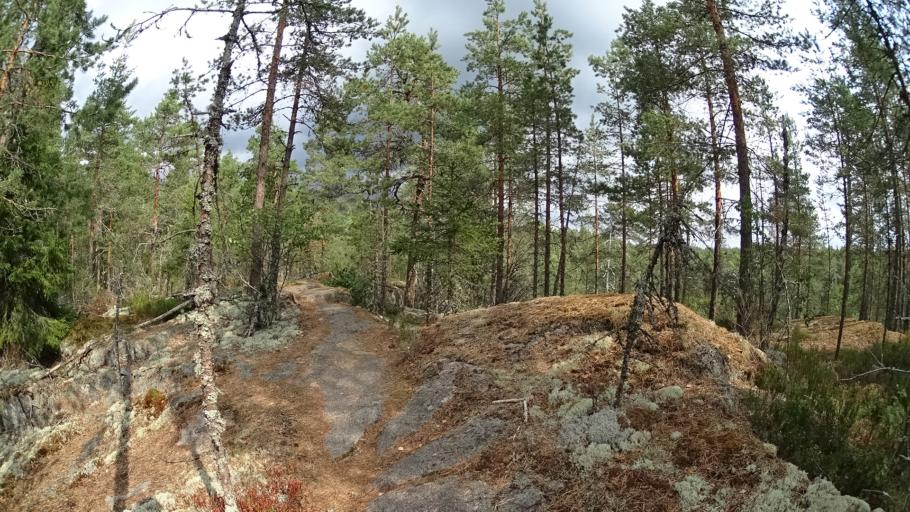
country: FI
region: Uusimaa
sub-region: Helsinki
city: Espoo
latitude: 60.3029
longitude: 24.5817
